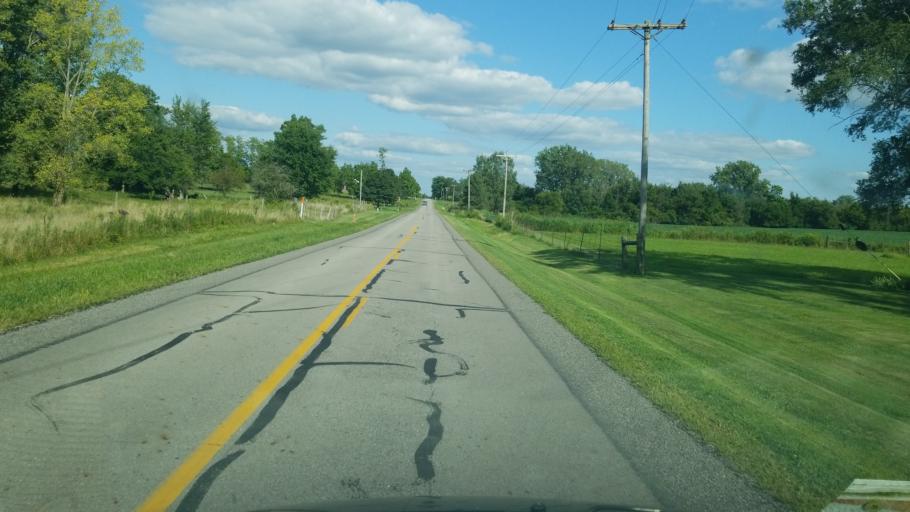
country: US
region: Ohio
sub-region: Champaign County
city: Saint Paris
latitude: 40.1564
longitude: -83.8859
